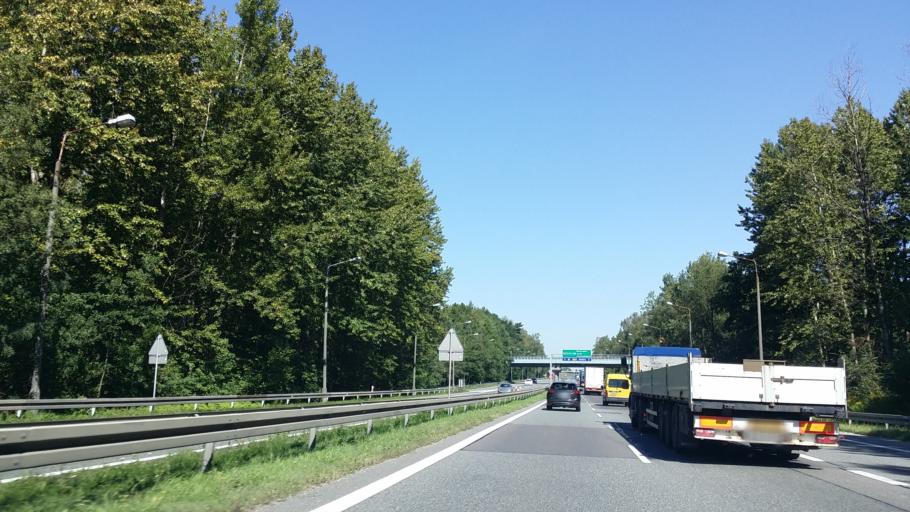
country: PL
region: Silesian Voivodeship
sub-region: Myslowice
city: Myslowice
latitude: 50.1802
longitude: 19.1681
